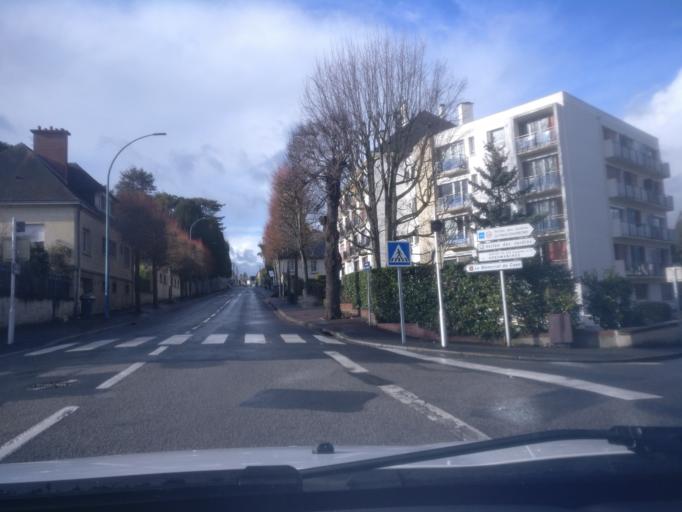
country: FR
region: Lower Normandy
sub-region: Departement du Calvados
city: Caen
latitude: 49.1895
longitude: -0.3707
